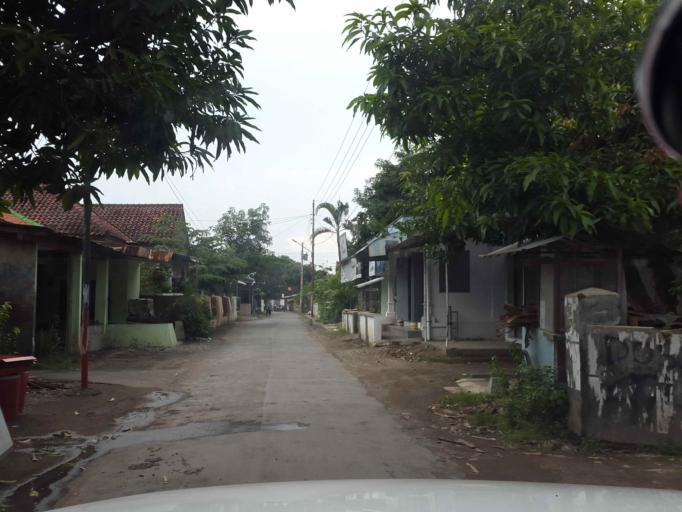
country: ID
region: Central Java
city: Tegal
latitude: -6.8949
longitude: 109.1291
